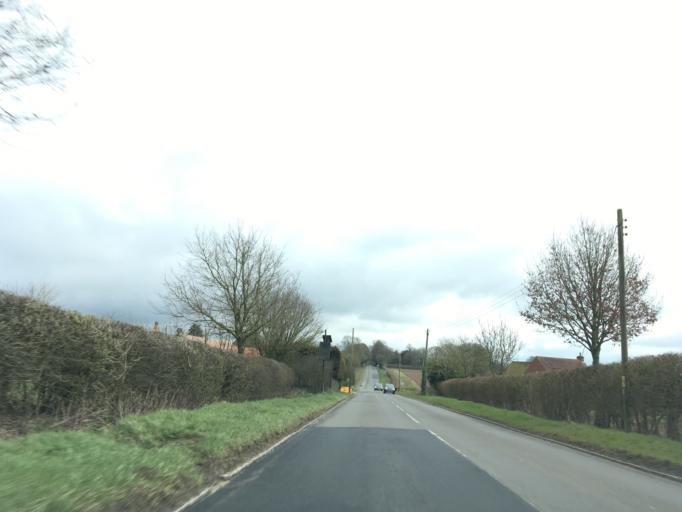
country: GB
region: England
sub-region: West Berkshire
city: Lambourn
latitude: 51.4761
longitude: -1.5283
